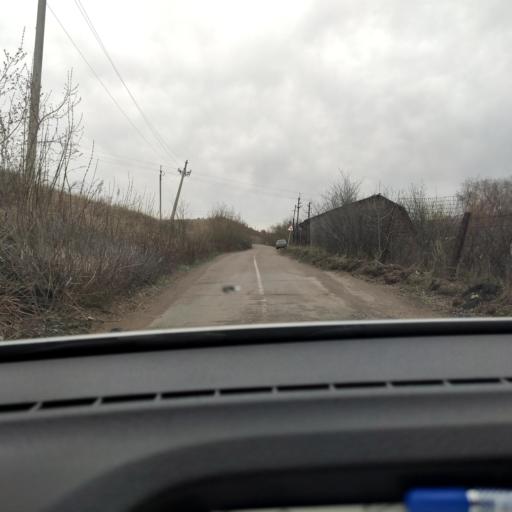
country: RU
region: Bashkortostan
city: Avdon
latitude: 54.6291
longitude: 55.5971
